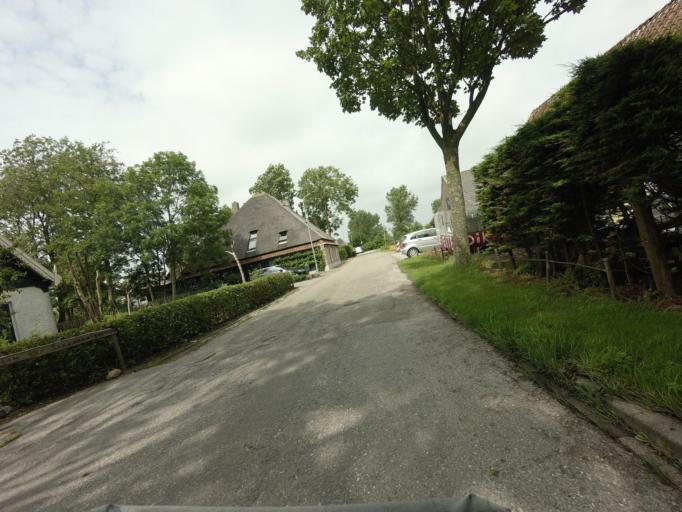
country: NL
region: North Holland
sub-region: Gemeente Schagen
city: Harenkarspel
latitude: 52.7386
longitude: 4.7595
